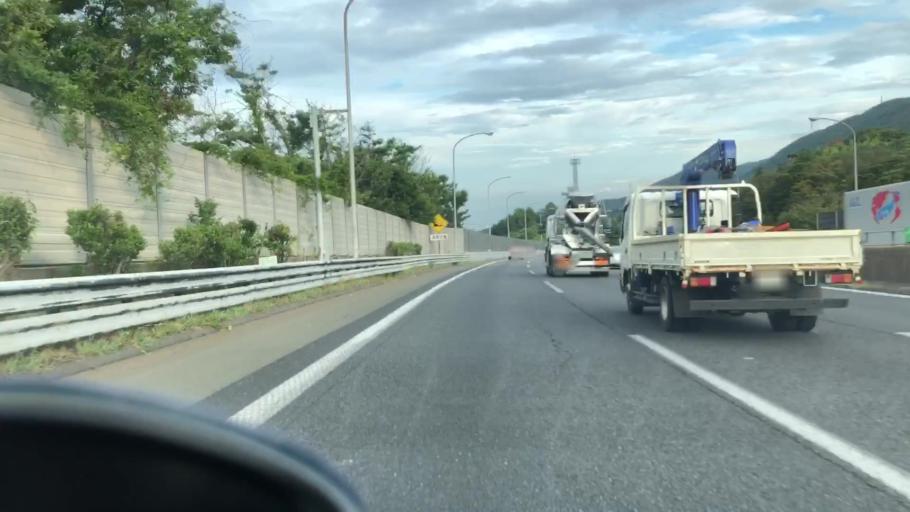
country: JP
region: Hyogo
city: Sandacho
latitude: 34.8345
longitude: 135.2795
